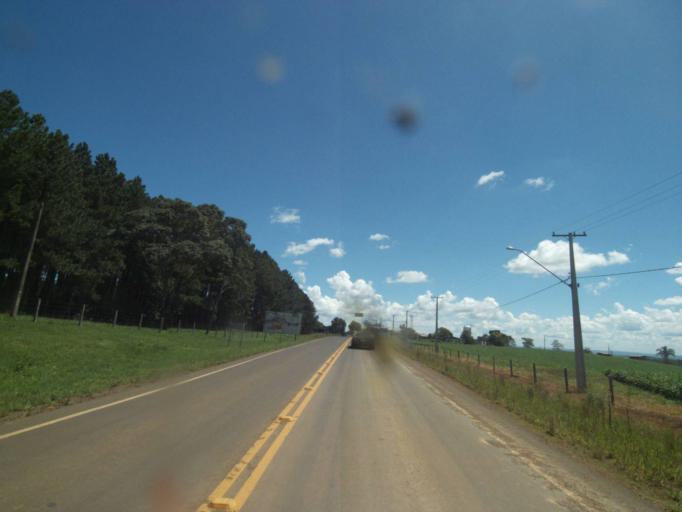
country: BR
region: Parana
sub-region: Pinhao
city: Pinhao
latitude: -25.8336
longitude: -52.0219
